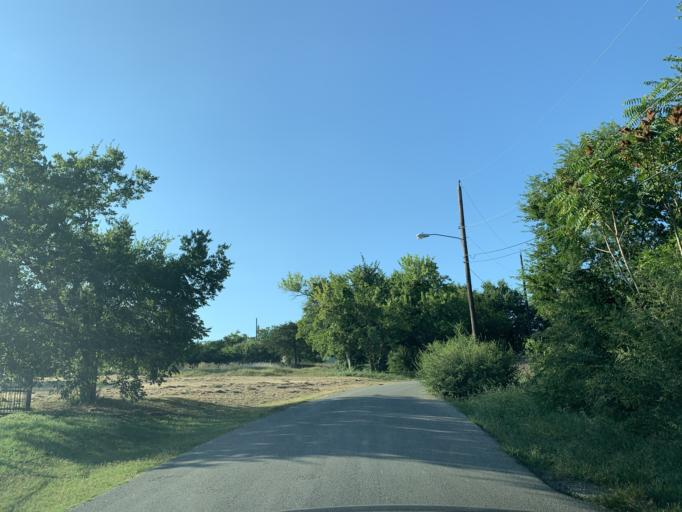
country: US
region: Texas
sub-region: Dallas County
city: Hutchins
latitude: 32.6700
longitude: -96.7768
